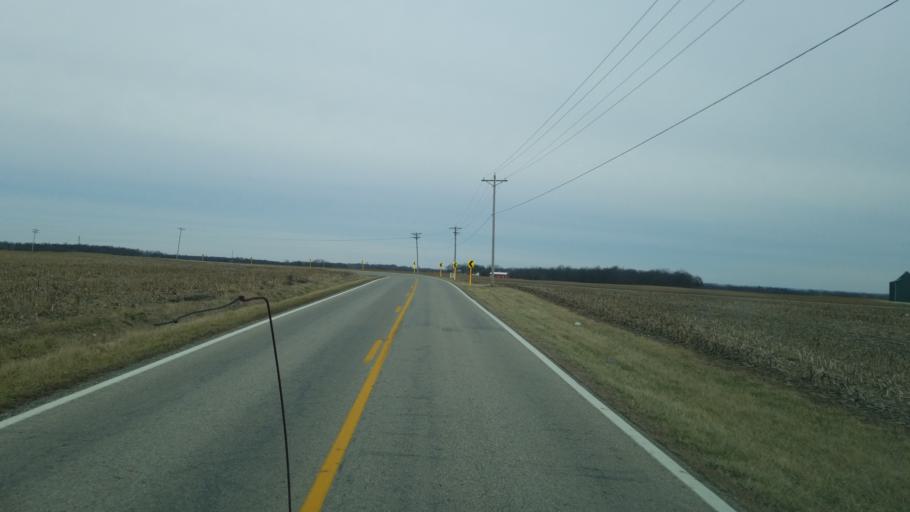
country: US
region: Ohio
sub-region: Pickaway County
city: Williamsport
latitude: 39.5256
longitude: -83.1271
